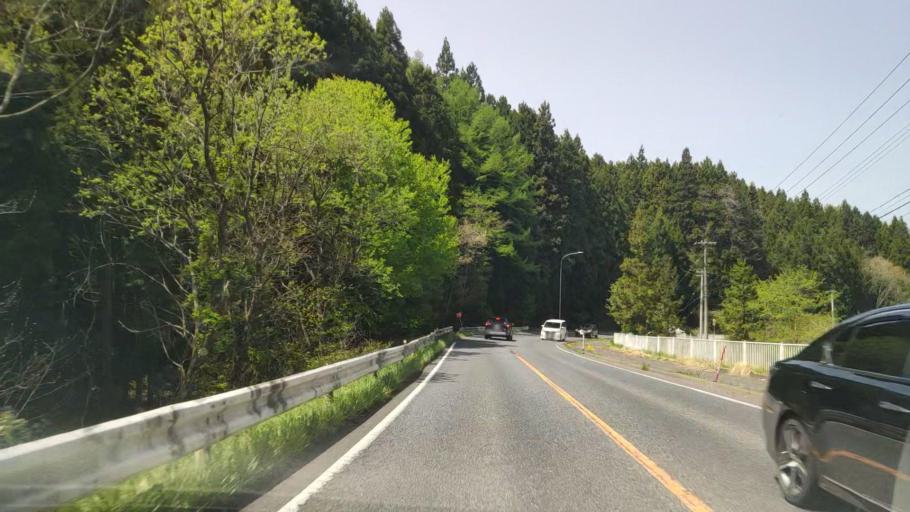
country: JP
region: Aomori
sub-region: Misawa Shi
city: Inuotose
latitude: 40.5832
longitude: 141.3574
